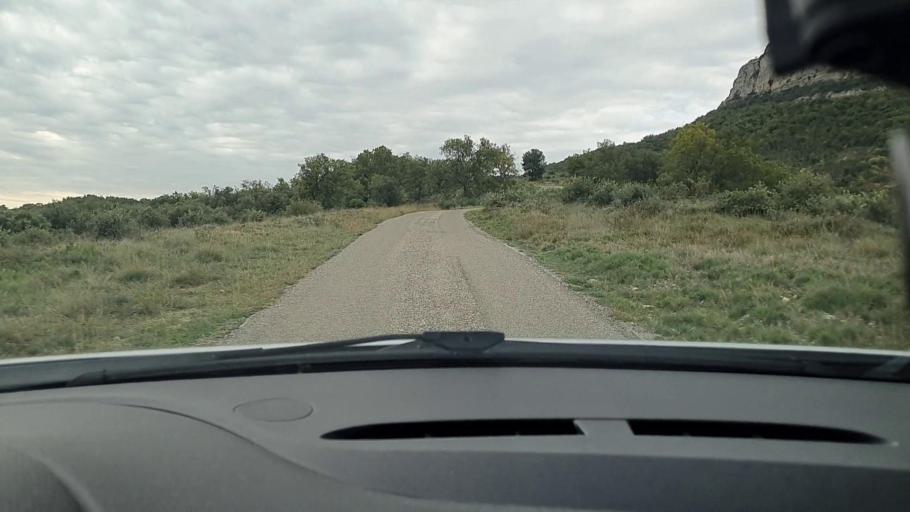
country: FR
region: Languedoc-Roussillon
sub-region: Departement du Gard
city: Mons
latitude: 44.1481
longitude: 4.2911
